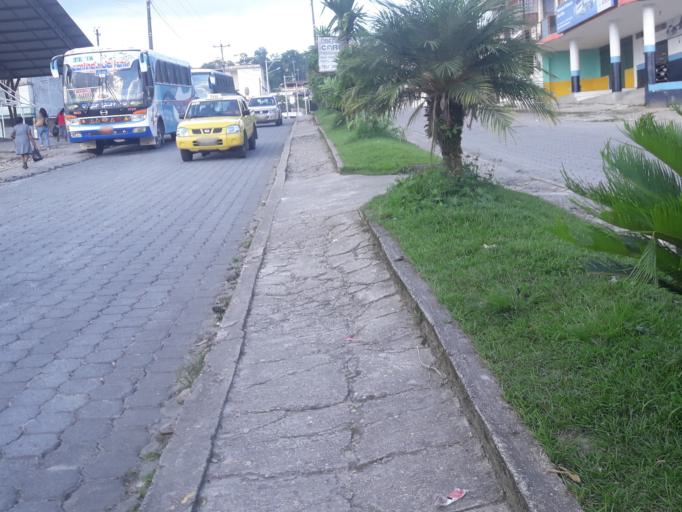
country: EC
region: Napo
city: Tena
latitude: -0.9994
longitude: -77.8103
